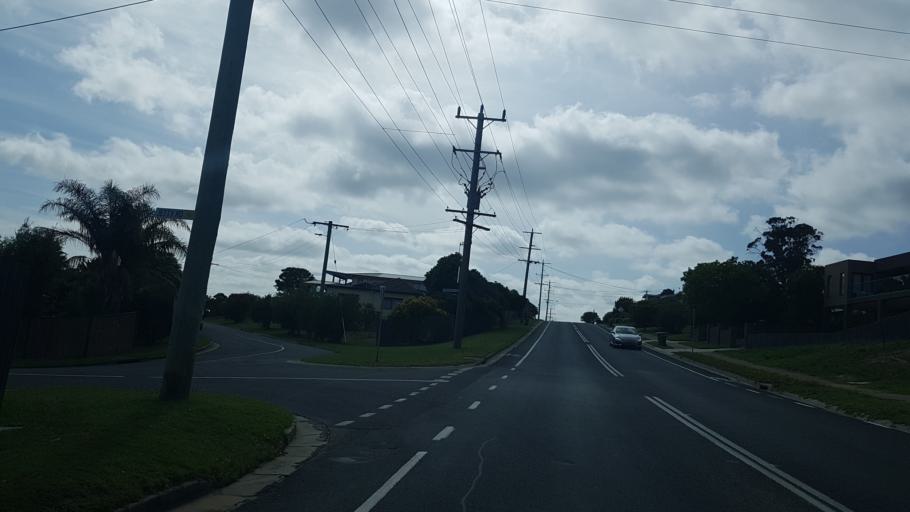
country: AU
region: Victoria
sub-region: Mornington Peninsula
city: Dromana
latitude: -38.3427
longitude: 144.9685
